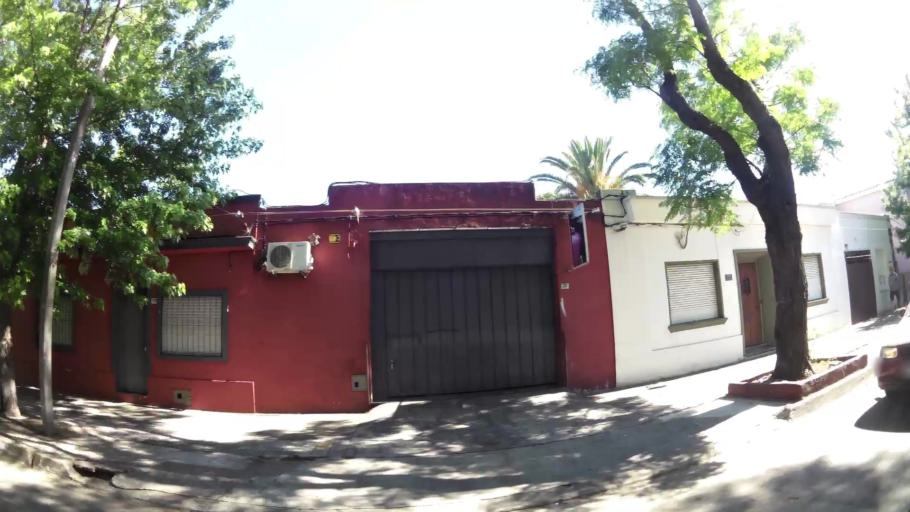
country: UY
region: Montevideo
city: Montevideo
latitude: -34.9016
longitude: -56.1498
